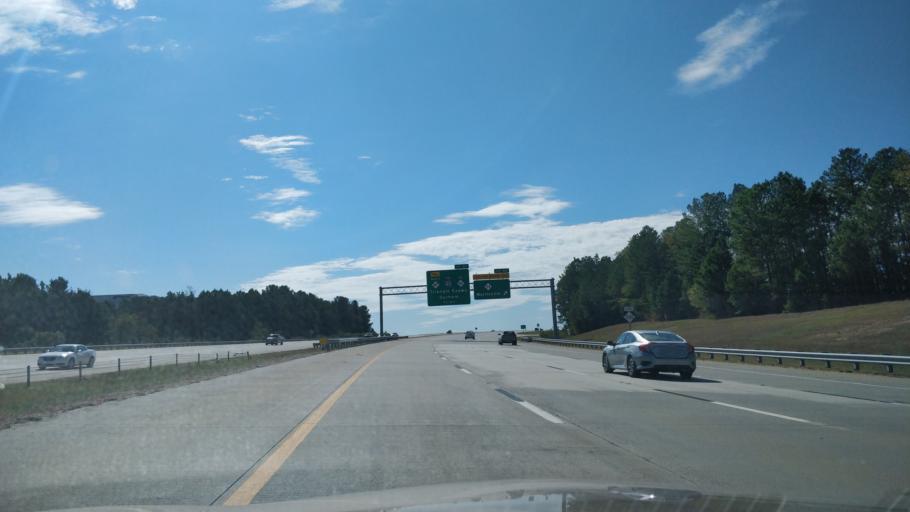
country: US
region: North Carolina
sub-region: Wake County
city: Morrisville
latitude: 35.8649
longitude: -78.8378
